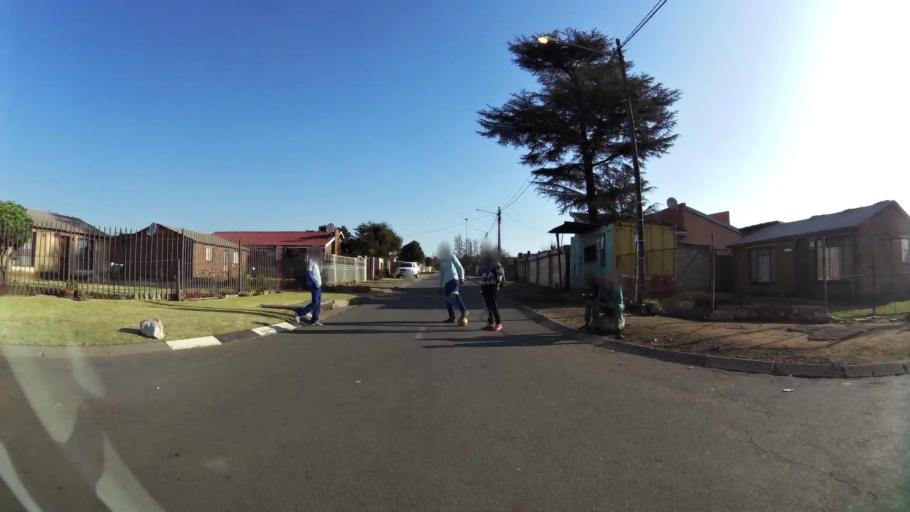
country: ZA
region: Gauteng
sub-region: City of Johannesburg Metropolitan Municipality
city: Soweto
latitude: -26.2645
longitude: 27.8746
